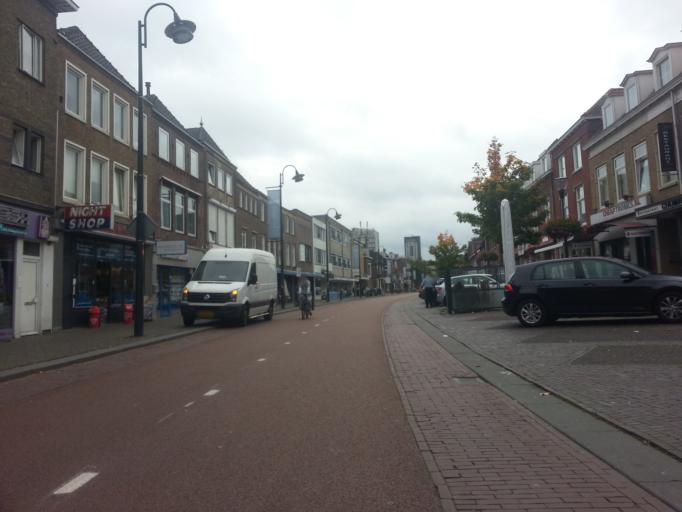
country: NL
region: North Brabant
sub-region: Gemeente Eindhoven
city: Eindhoven
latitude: 51.4476
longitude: 5.4754
